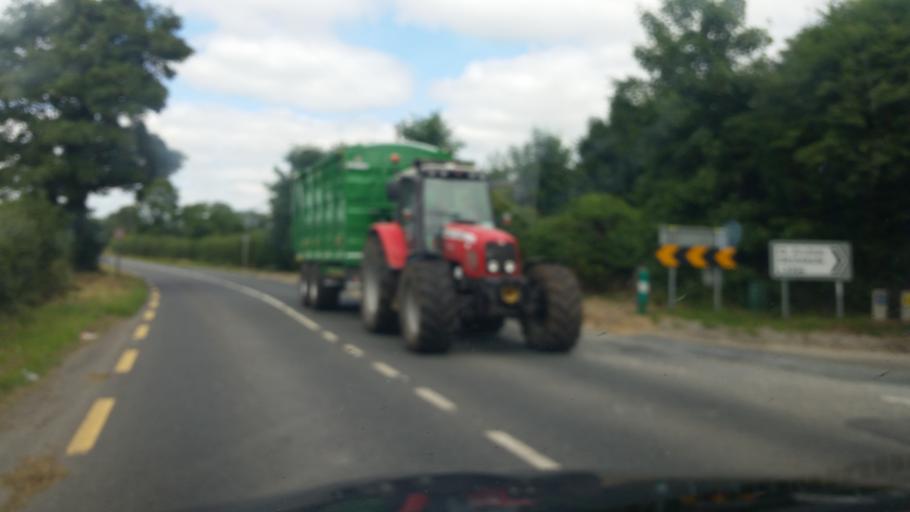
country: IE
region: Leinster
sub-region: Wicklow
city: Baltinglass
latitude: 52.9596
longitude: -6.6992
